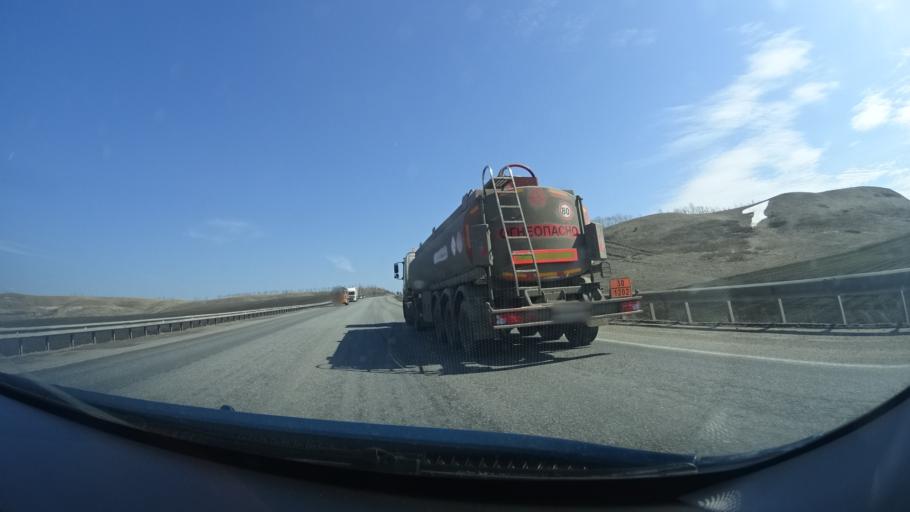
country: RU
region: Bashkortostan
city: Serafimovskiy
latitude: 54.4708
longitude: 53.7643
